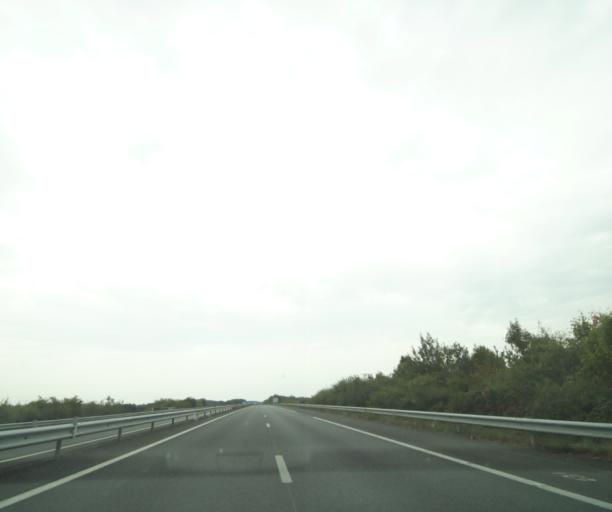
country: FR
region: Pays de la Loire
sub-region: Departement de la Vendee
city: Bournezeau
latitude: 46.6415
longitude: -1.1506
